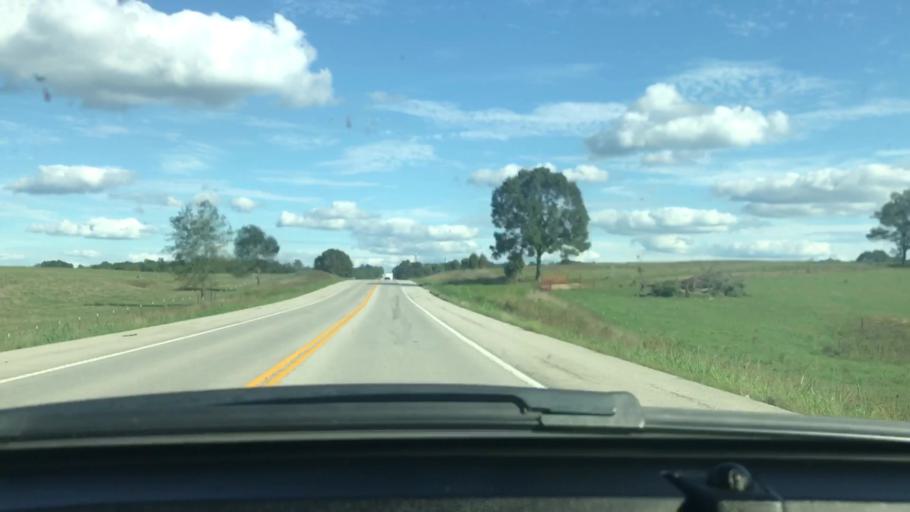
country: US
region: Missouri
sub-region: Howell County
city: West Plains
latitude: 36.6574
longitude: -91.7021
